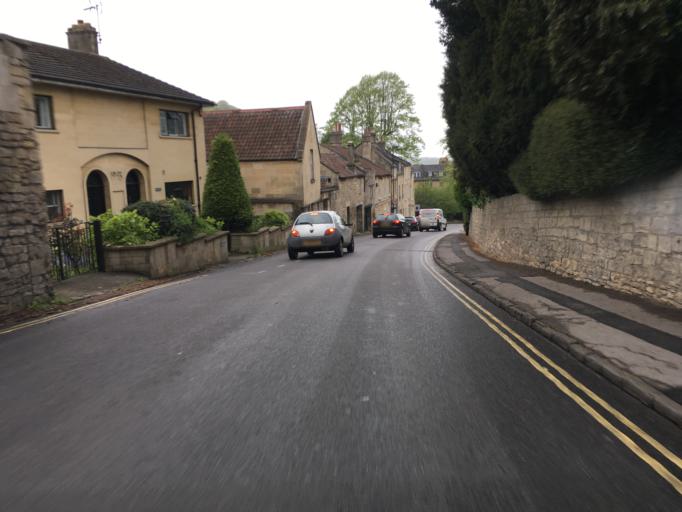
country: GB
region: England
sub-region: Bath and North East Somerset
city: Bath
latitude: 51.3749
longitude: -2.3480
